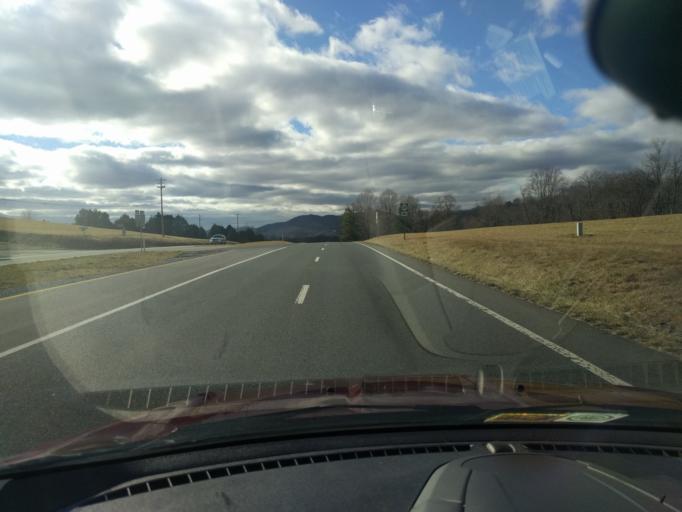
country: US
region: Virginia
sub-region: City of Bedford
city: Bedford
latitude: 37.3510
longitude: -79.6316
